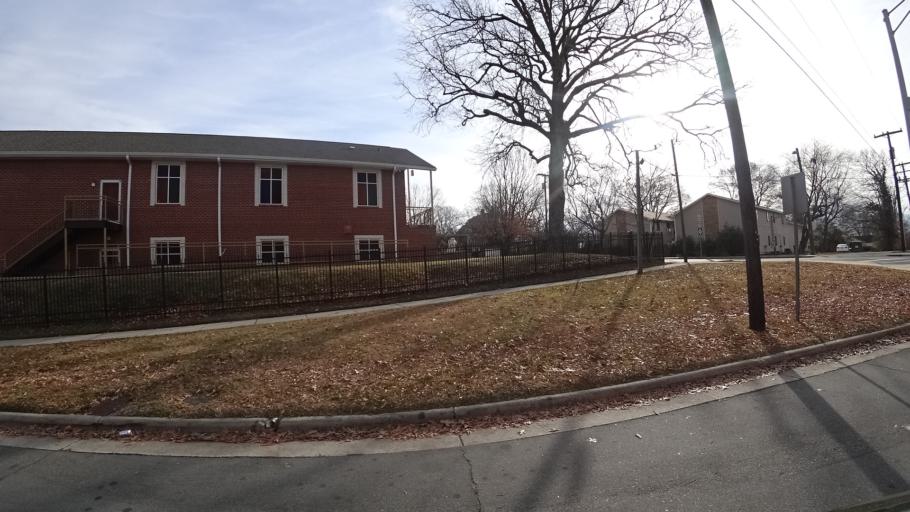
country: US
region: North Carolina
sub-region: Durham County
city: Durham
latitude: 35.9947
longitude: -78.8935
